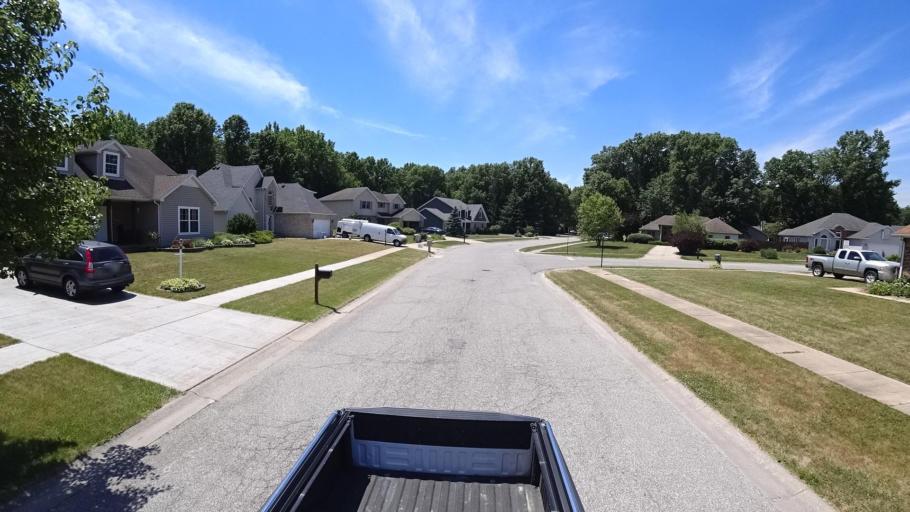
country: US
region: Indiana
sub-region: Porter County
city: Porter
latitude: 41.6018
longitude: -87.0953
